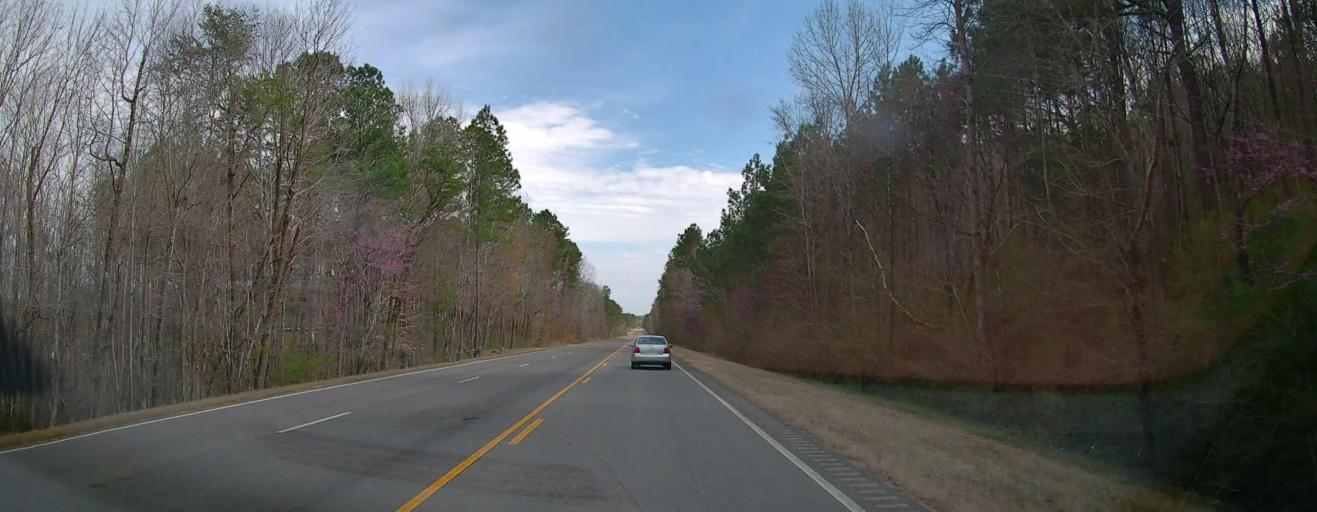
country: US
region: Alabama
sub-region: Walker County
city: Carbon Hill
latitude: 33.9132
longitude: -87.5625
